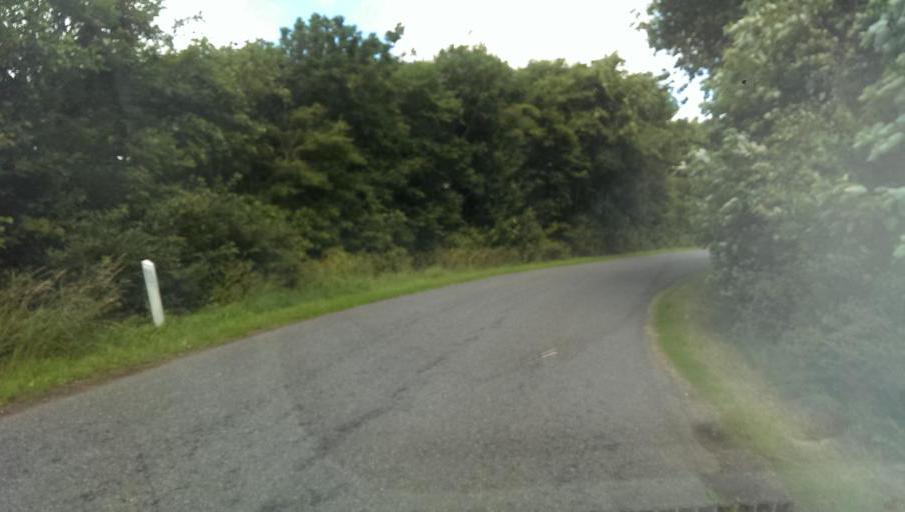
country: DK
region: Central Jutland
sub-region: Holstebro Kommune
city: Ulfborg
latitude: 56.2586
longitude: 8.2379
